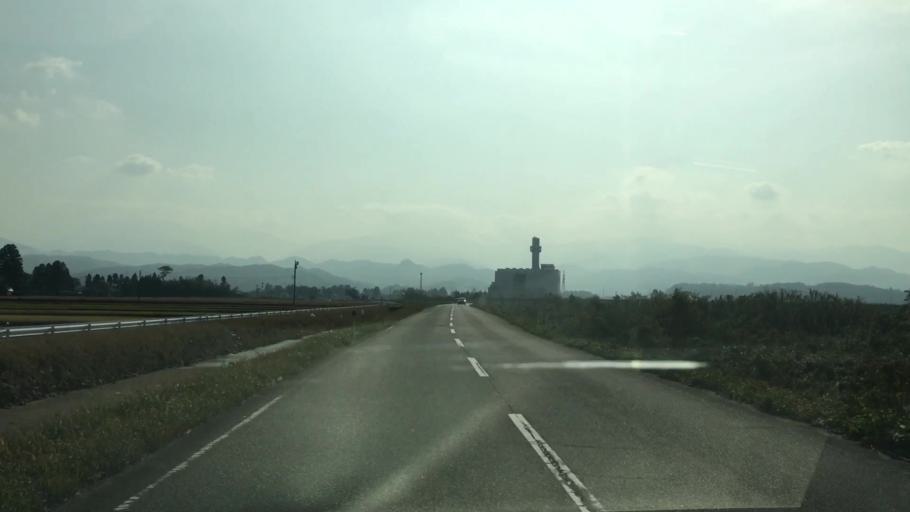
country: JP
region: Toyama
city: Kamiichi
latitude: 36.6319
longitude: 137.2960
